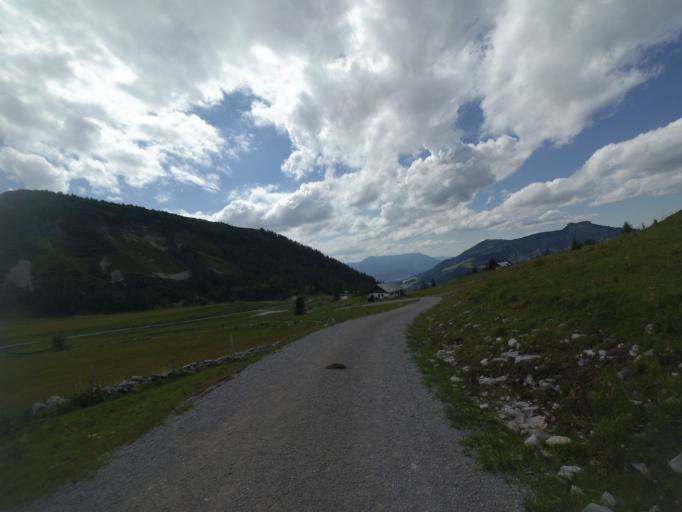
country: AT
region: Salzburg
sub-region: Politischer Bezirk Salzburg-Umgebung
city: Hintersee
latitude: 47.6510
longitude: 13.2832
